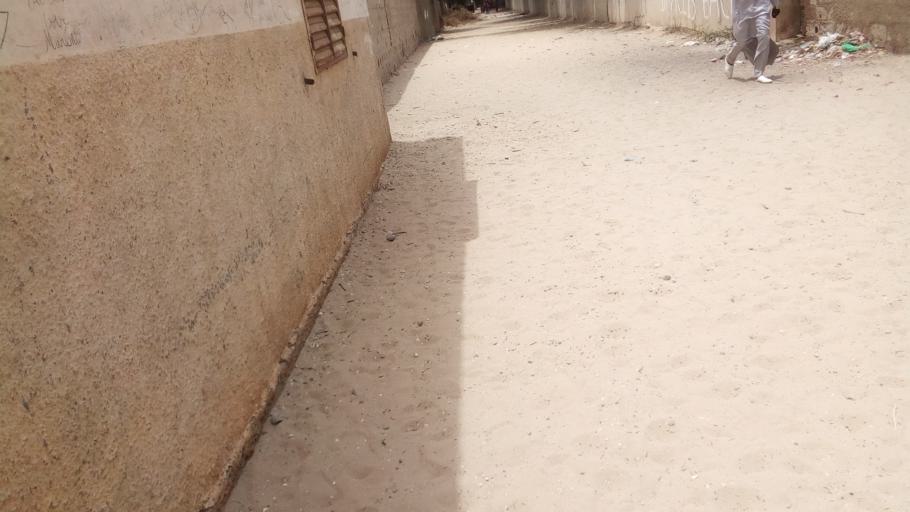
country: SN
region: Saint-Louis
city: Saint-Louis
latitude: 16.0171
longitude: -16.4875
